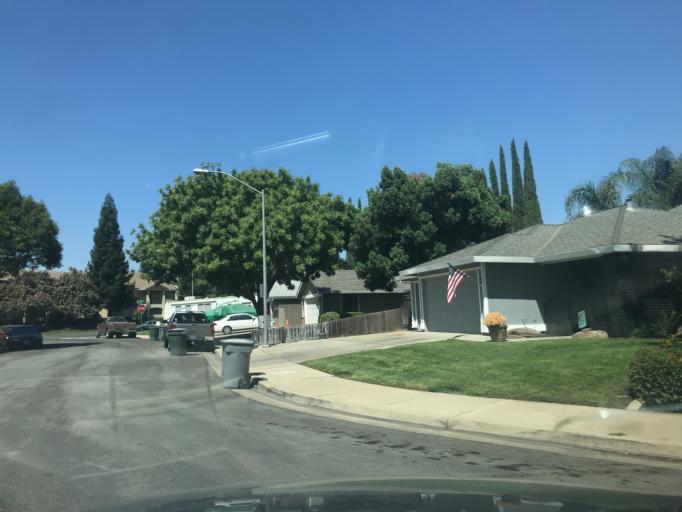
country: US
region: California
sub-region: Merced County
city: Merced
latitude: 37.3345
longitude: -120.4824
